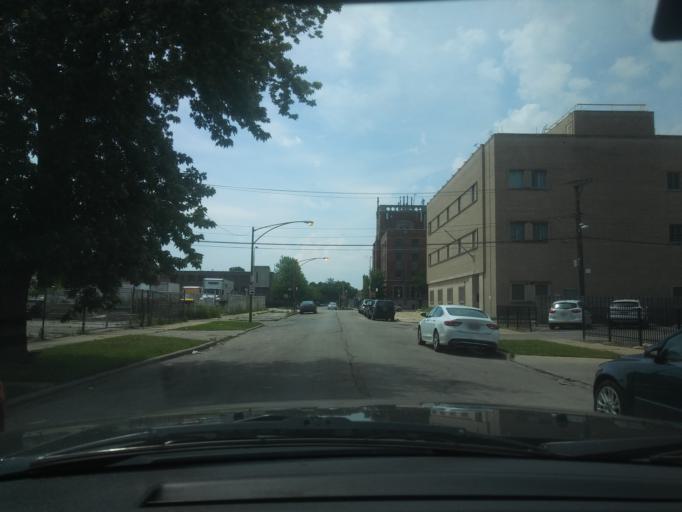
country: US
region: Illinois
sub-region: Cook County
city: Evergreen Park
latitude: 41.7800
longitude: -87.6824
